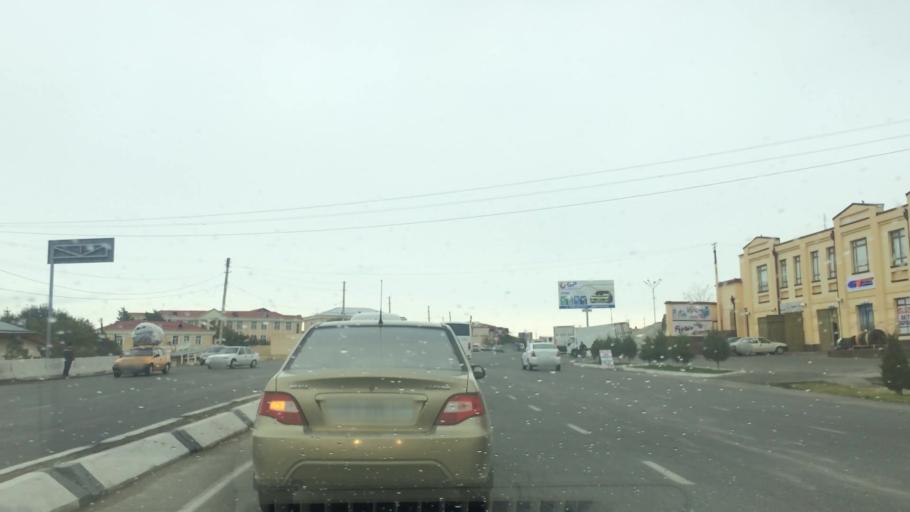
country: UZ
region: Samarqand
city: Samarqand
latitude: 39.6775
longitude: 67.0060
